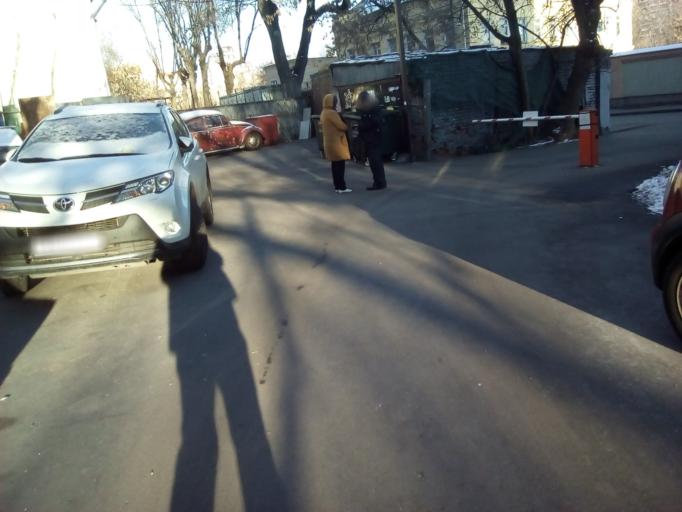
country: RU
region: Moskovskaya
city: Dorogomilovo
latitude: 55.7626
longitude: 37.5738
